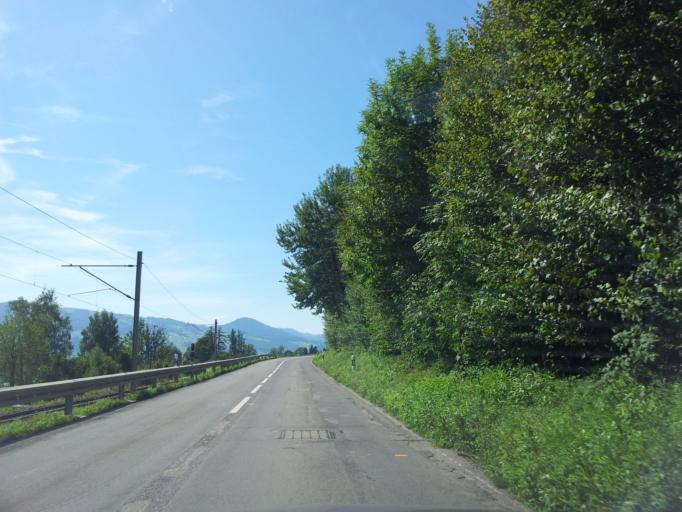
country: CH
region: Saint Gallen
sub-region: Wahlkreis See-Gaster
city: Eschenbach
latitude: 47.2187
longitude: 8.8894
